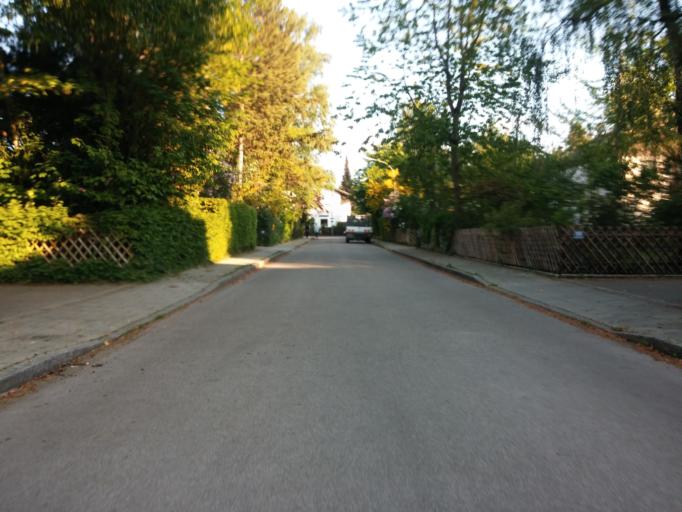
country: DE
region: Bavaria
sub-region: Upper Bavaria
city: Vaterstetten
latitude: 48.1032
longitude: 11.7817
